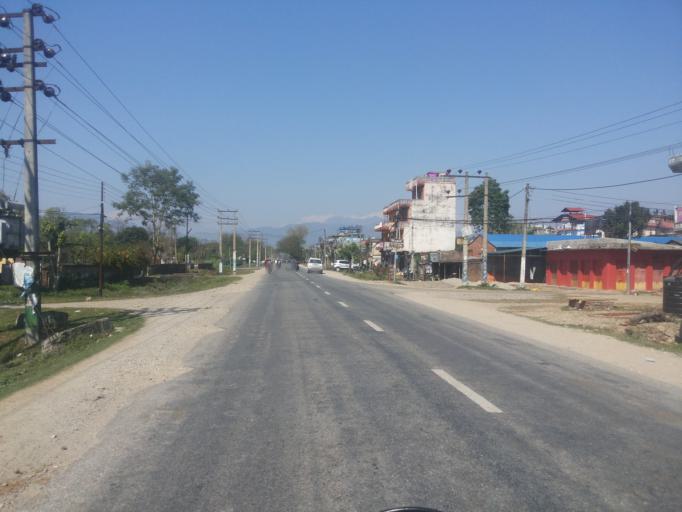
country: NP
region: Central Region
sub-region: Narayani Zone
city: Bharatpur
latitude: 27.6775
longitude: 84.4390
